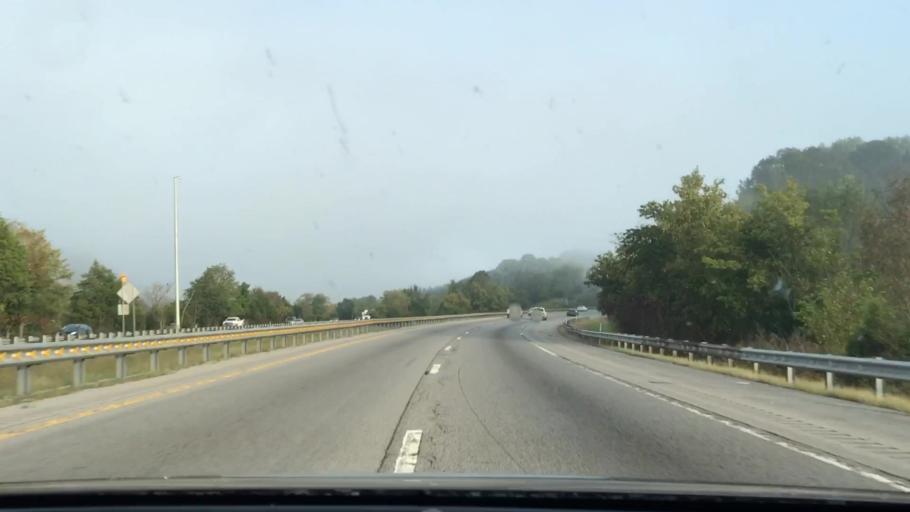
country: US
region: Tennessee
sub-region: Sumner County
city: Millersville
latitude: 36.4005
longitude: -86.7191
